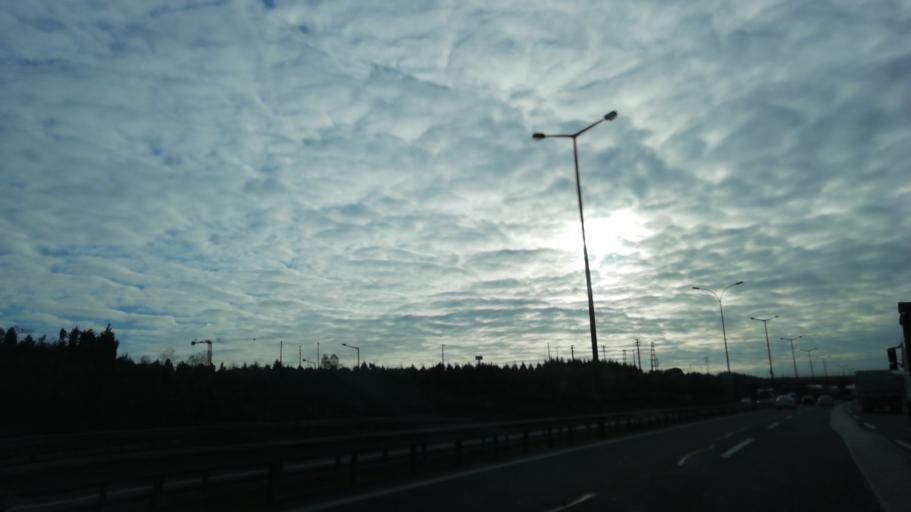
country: TR
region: Kocaeli
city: Balcik
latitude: 40.8699
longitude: 29.3963
